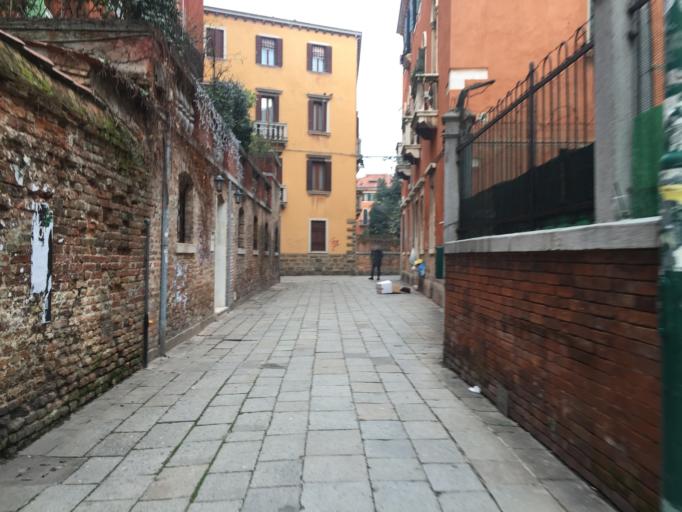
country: IT
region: Veneto
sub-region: Provincia di Venezia
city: Venice
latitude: 45.4374
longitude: 12.3247
